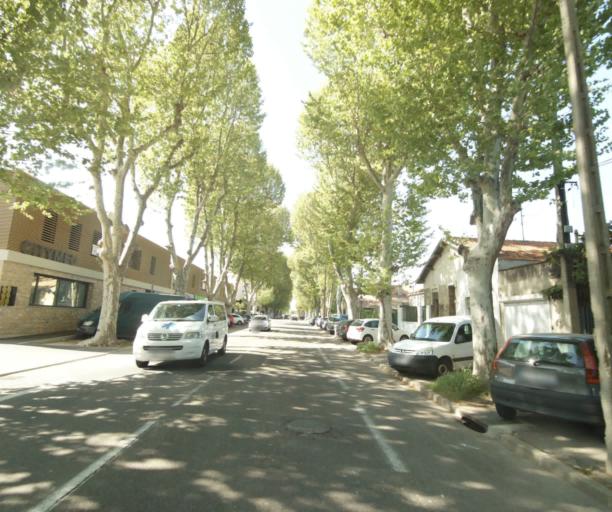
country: FR
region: Languedoc-Roussillon
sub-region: Departement de l'Herault
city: Montpellier
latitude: 43.6141
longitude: 3.8581
